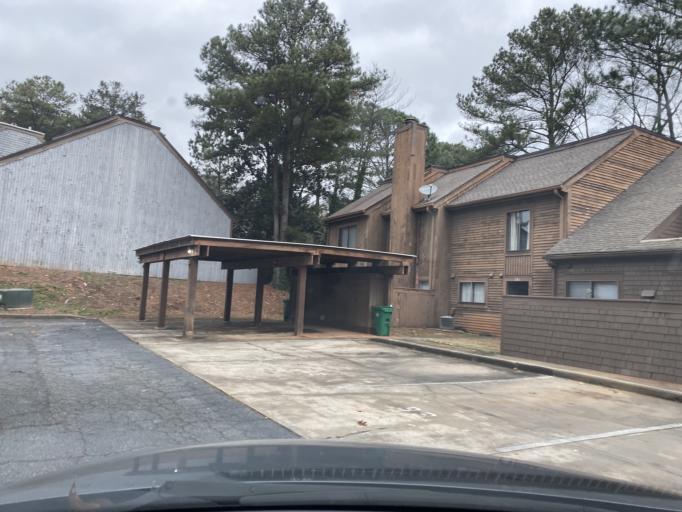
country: US
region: Georgia
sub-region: DeKalb County
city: Pine Mountain
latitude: 33.7016
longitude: -84.1526
